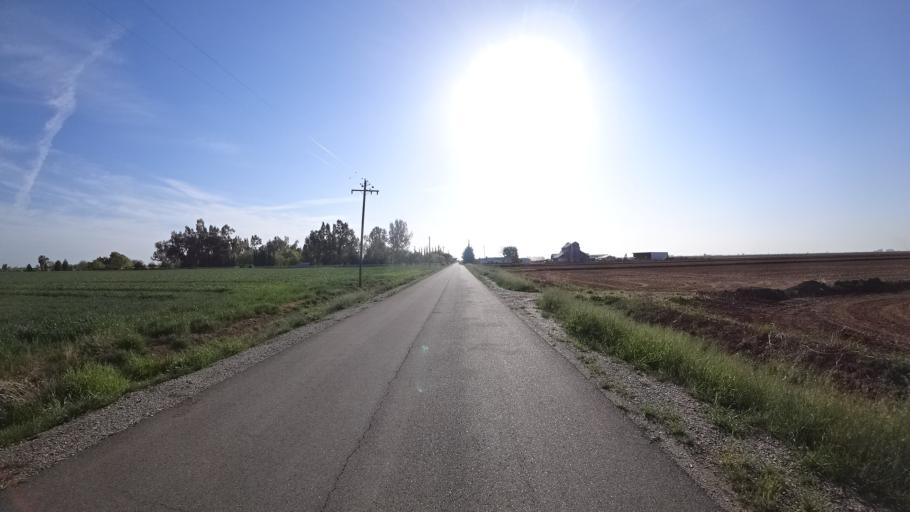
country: US
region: California
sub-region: Glenn County
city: Willows
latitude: 39.5095
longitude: -122.2286
